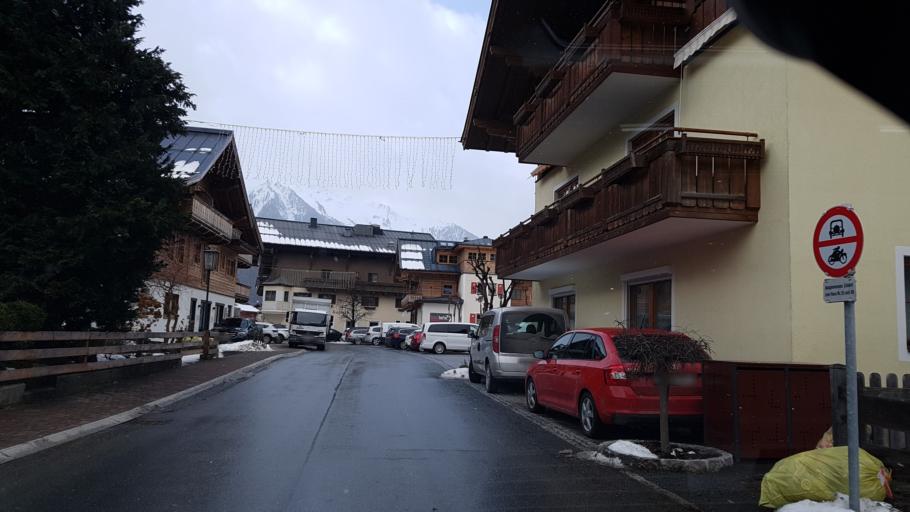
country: AT
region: Salzburg
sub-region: Politischer Bezirk Zell am See
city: Bramberg am Wildkogel
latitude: 47.2737
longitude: 12.3486
